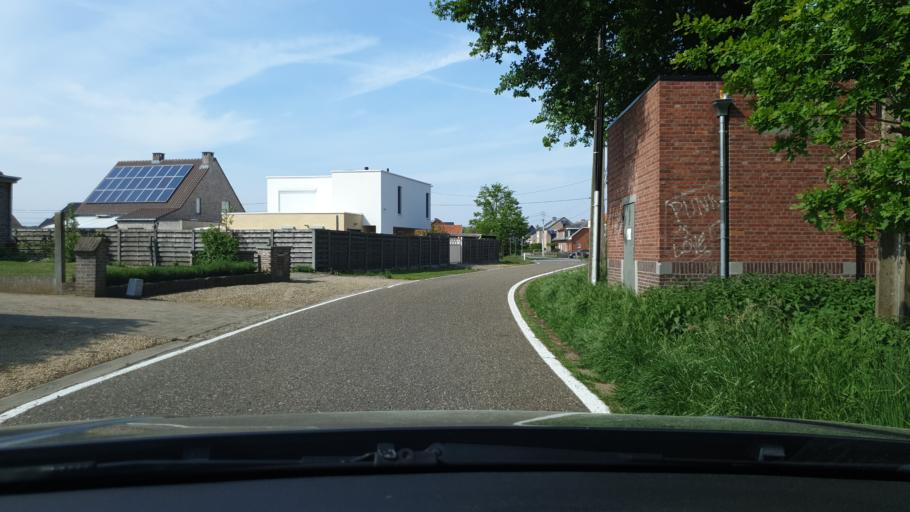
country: BE
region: Flanders
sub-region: Provincie Antwerpen
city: Laakdal
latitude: 51.0791
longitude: 5.0406
